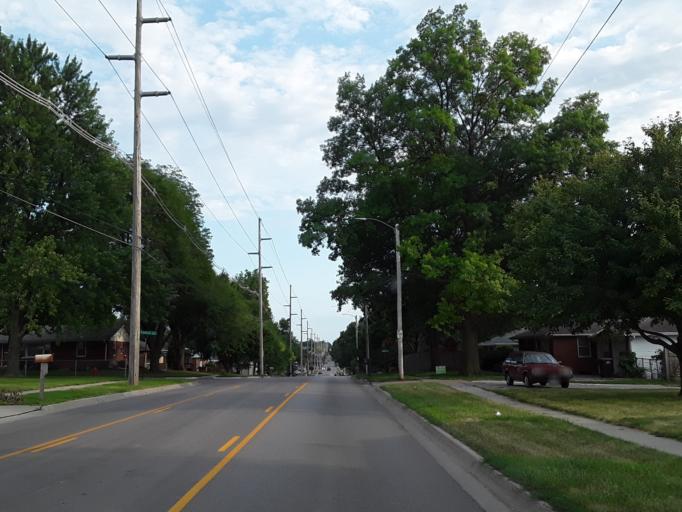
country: US
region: Nebraska
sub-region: Lancaster County
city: Lincoln
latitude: 40.8323
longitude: -96.6442
